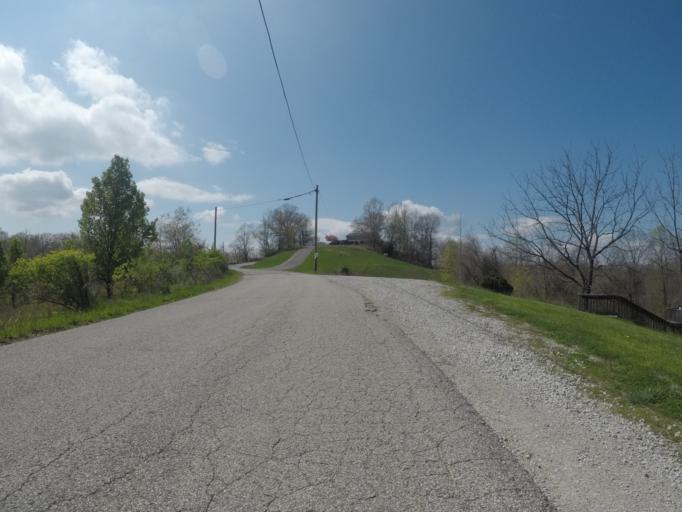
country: US
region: Ohio
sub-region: Lawrence County
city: Burlington
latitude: 38.3859
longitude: -82.5331
